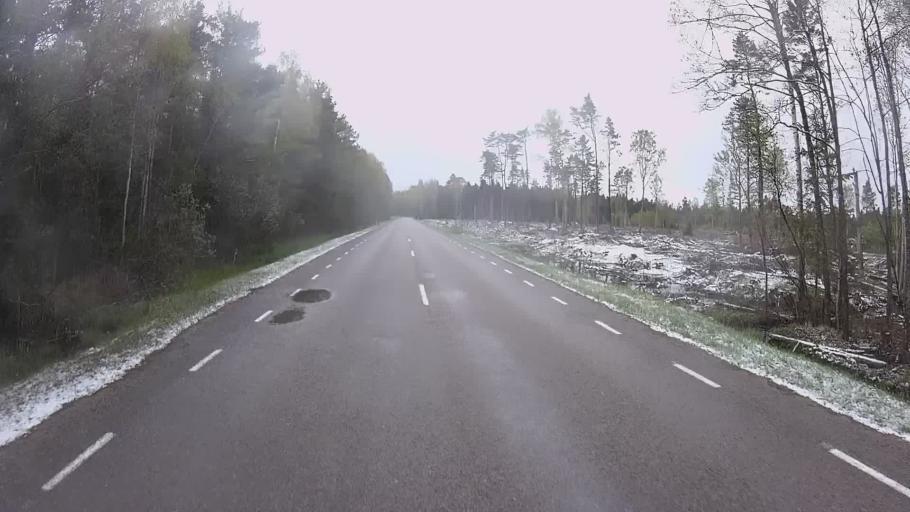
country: EE
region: Hiiumaa
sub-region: Kaerdla linn
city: Kardla
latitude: 58.8267
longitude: 22.4692
